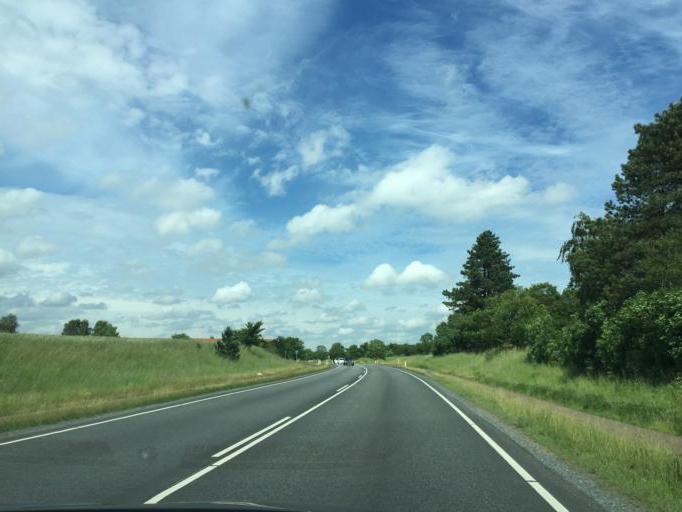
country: DK
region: South Denmark
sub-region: Odense Kommune
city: Hojby
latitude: 55.3169
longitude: 10.4041
